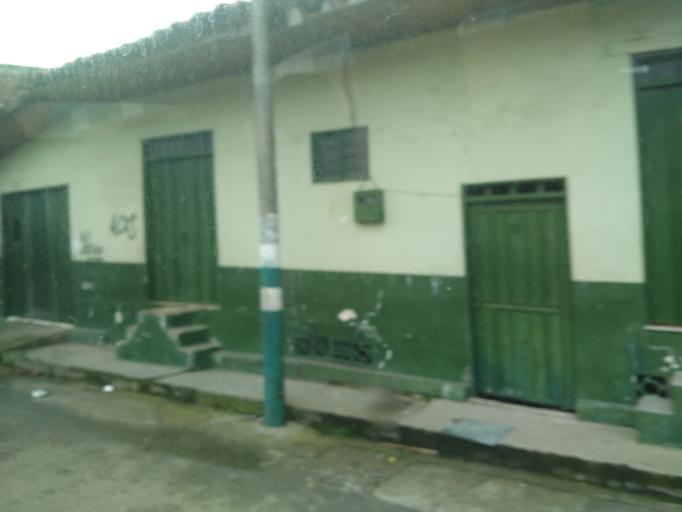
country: CO
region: Valle del Cauca
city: Sevilla
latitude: 4.2663
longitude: -75.9315
